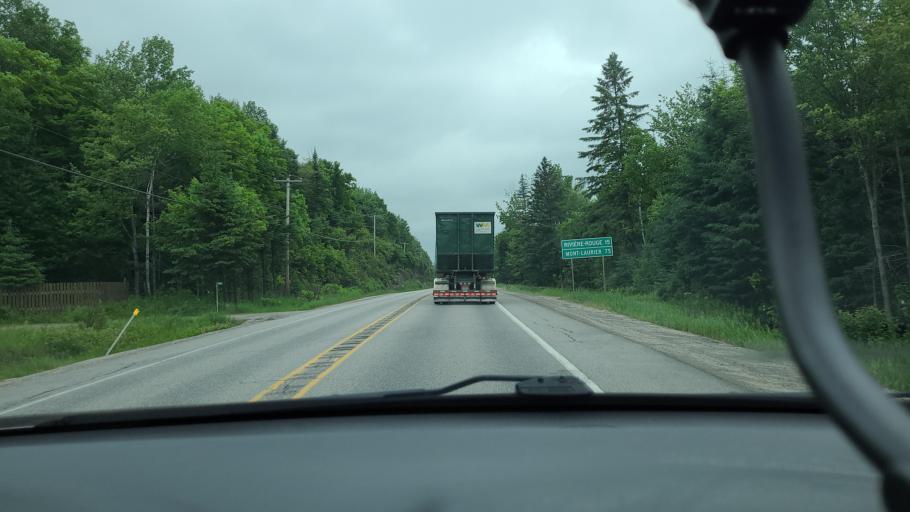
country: CA
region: Quebec
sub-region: Laurentides
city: Labelle
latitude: 46.3022
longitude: -74.7830
